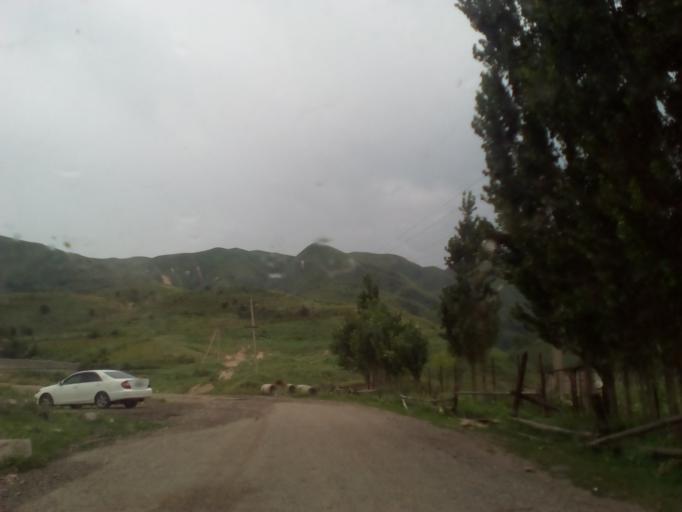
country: KZ
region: Almaty Oblysy
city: Burunday
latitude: 43.1505
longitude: 76.3855
